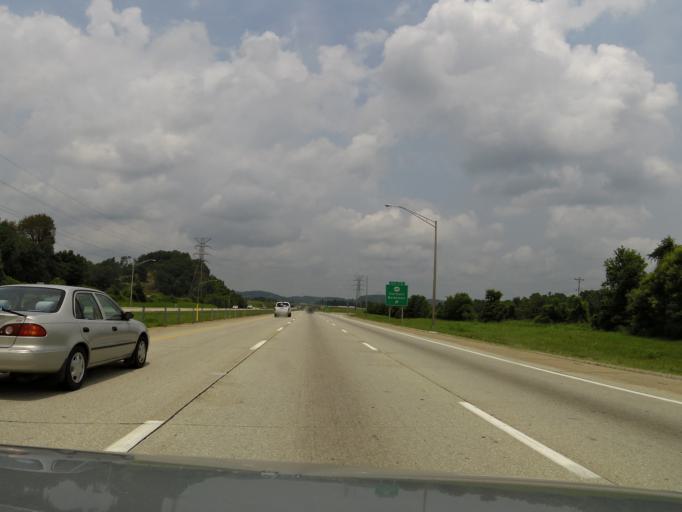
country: US
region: Kentucky
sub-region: Bullitt County
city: Shepherdsville
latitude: 37.9187
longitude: -85.6871
